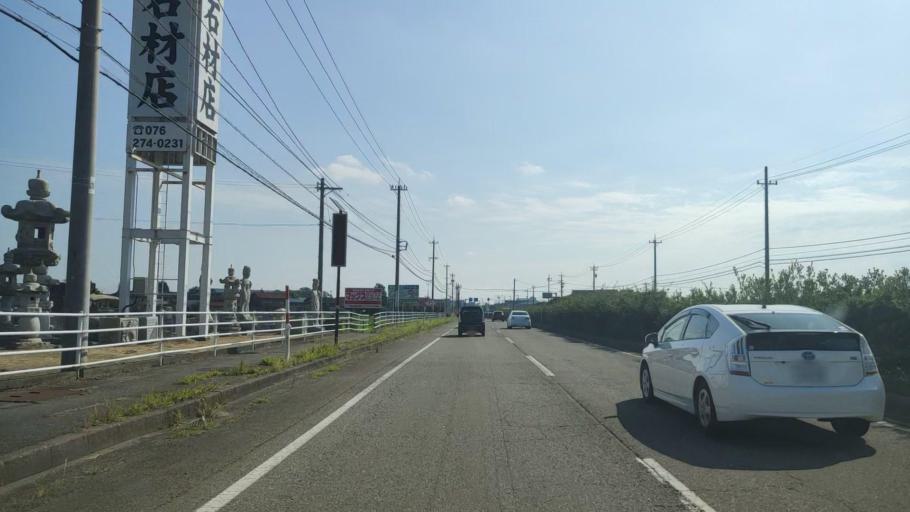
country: JP
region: Ishikawa
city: Matsuto
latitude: 36.5039
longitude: 136.5493
